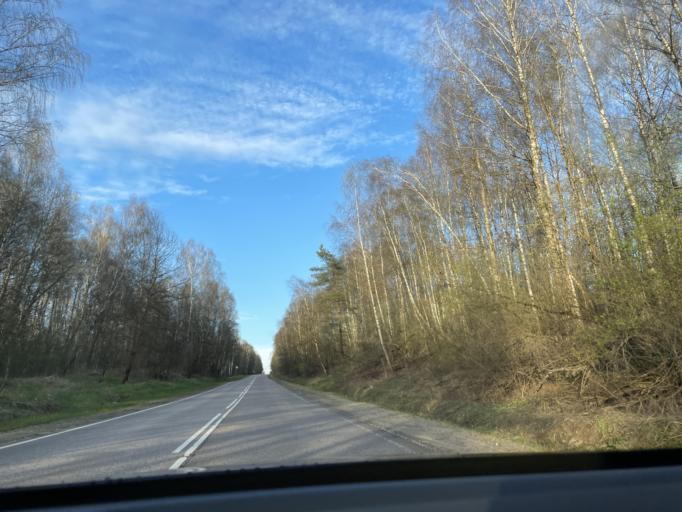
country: RU
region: Tula
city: Novogurovskiy
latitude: 54.5239
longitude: 37.2711
